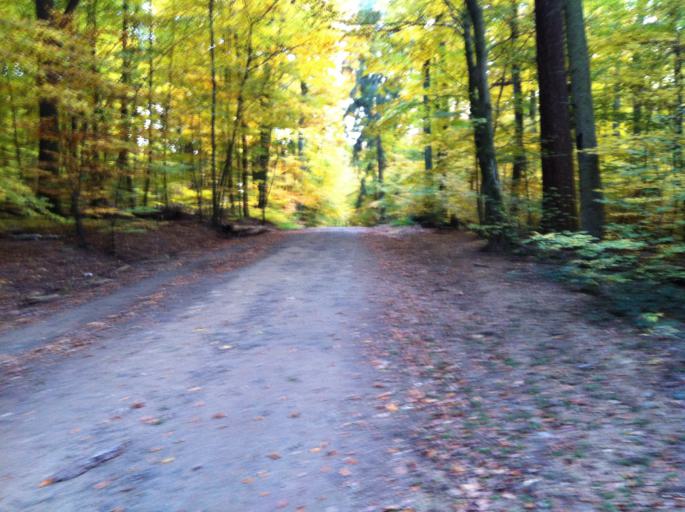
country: DE
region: Hesse
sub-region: Regierungsbezirk Darmstadt
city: Wiesbaden
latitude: 50.1071
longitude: 8.2346
